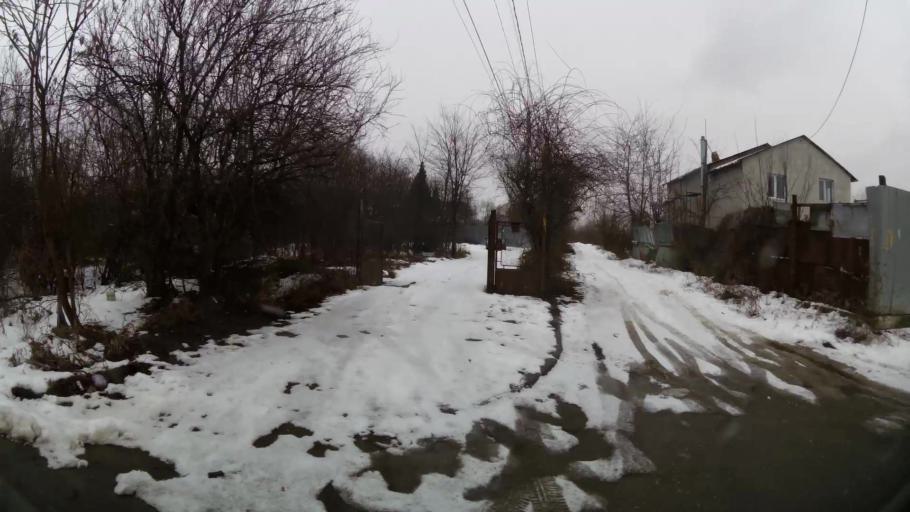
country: RO
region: Ilfov
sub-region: Comuna Mogosoaia
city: Mogosoaia
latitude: 44.5123
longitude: 26.0280
